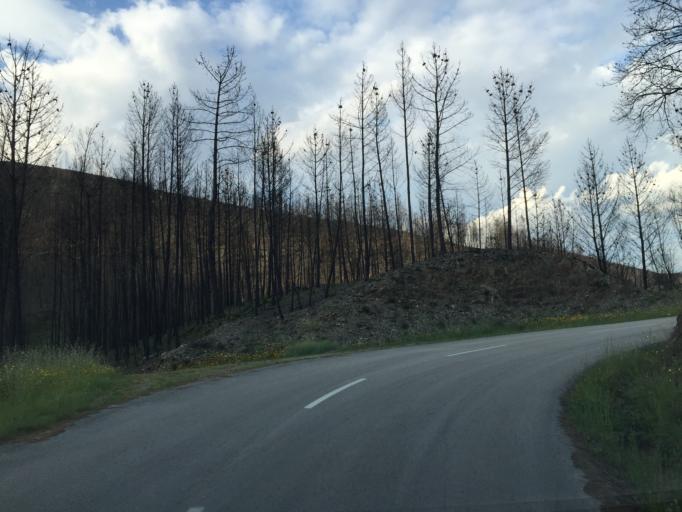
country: PT
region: Coimbra
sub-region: Arganil
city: Arganil
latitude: 40.1401
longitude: -7.9970
